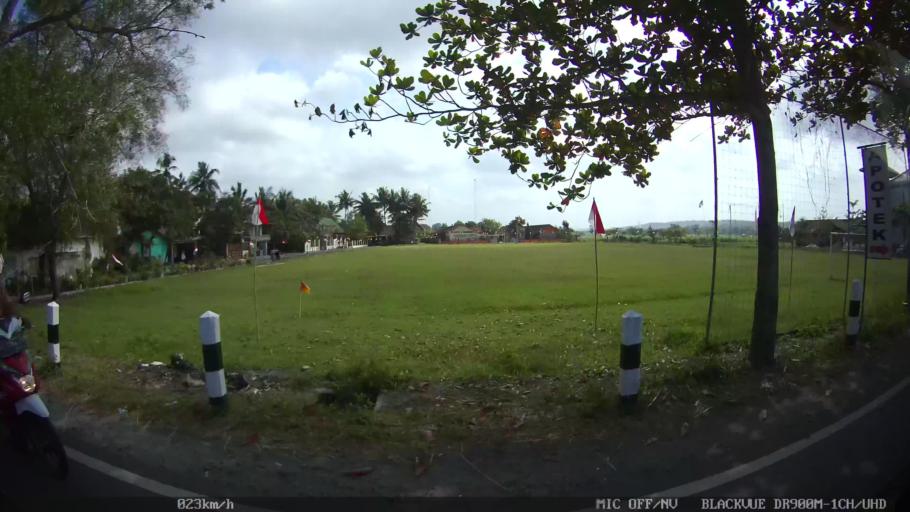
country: ID
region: Daerah Istimewa Yogyakarta
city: Srandakan
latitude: -7.8939
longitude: 110.1448
